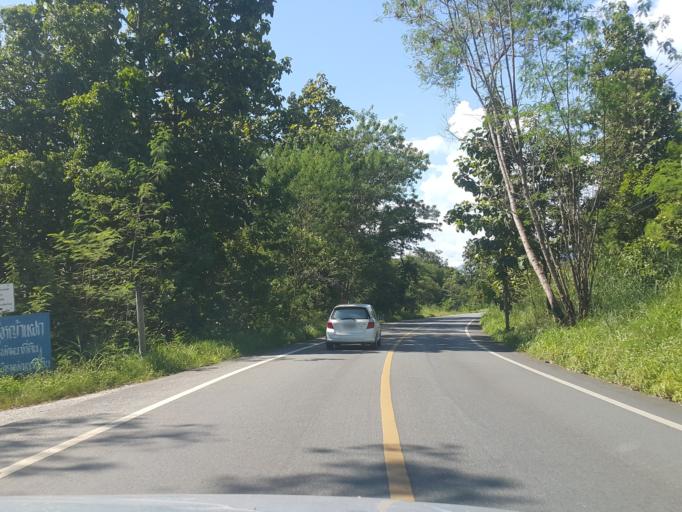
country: TH
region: Chiang Mai
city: Mae Taeng
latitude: 19.1642
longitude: 98.9334
